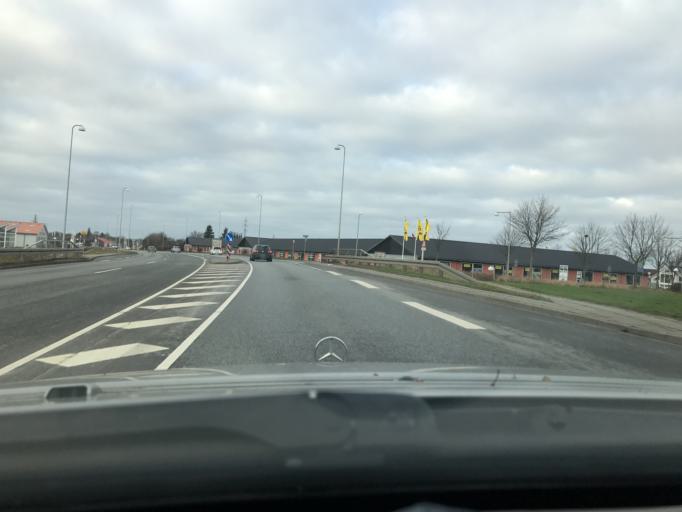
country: DK
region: South Denmark
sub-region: Aabenraa Kommune
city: Rodekro
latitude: 55.0694
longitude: 9.3569
